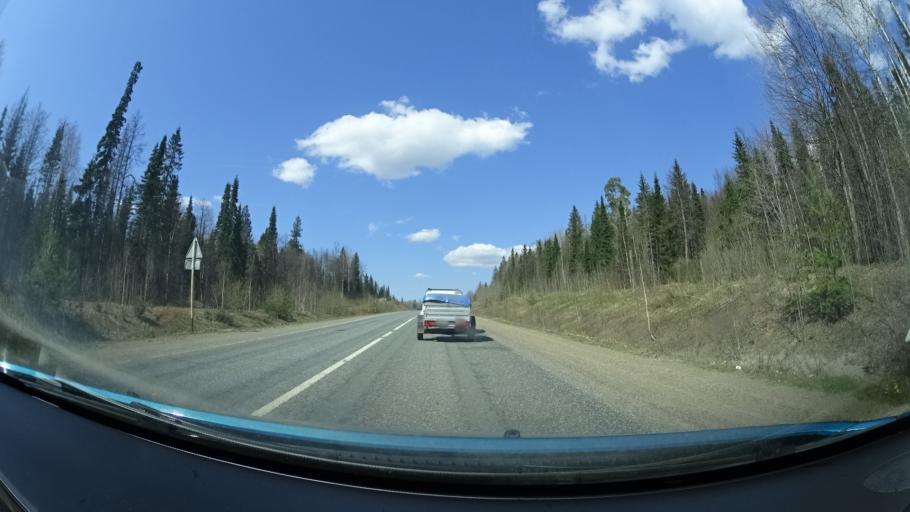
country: RU
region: Perm
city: Yugo-Kamskiy
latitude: 57.6207
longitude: 55.6217
